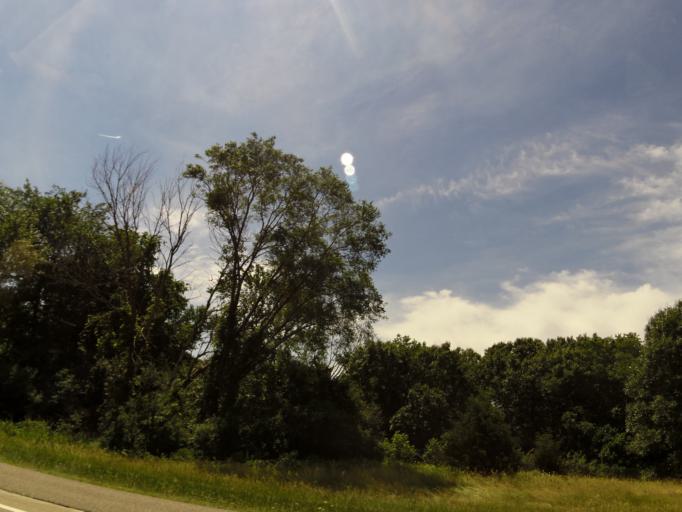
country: US
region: Minnesota
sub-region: Scott County
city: Prior Lake
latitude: 44.7829
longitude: -93.4255
